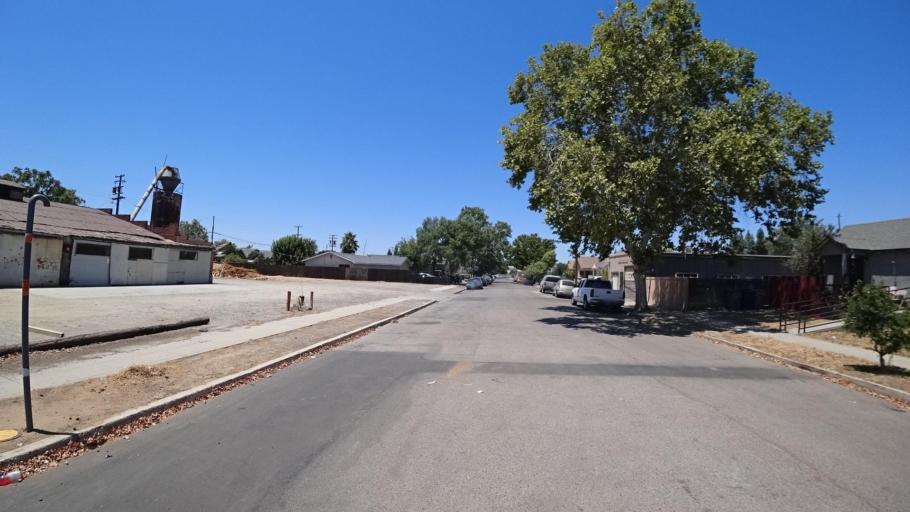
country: US
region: California
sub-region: Fresno County
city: Fresno
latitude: 36.7563
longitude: -119.7876
